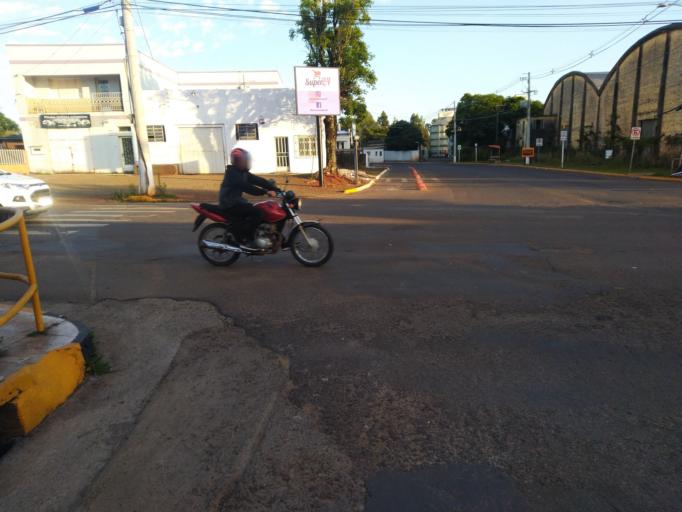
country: BR
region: Rio Grande do Sul
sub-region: Sao Borja
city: Sao Borja
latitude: -28.6500
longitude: -56.0071
